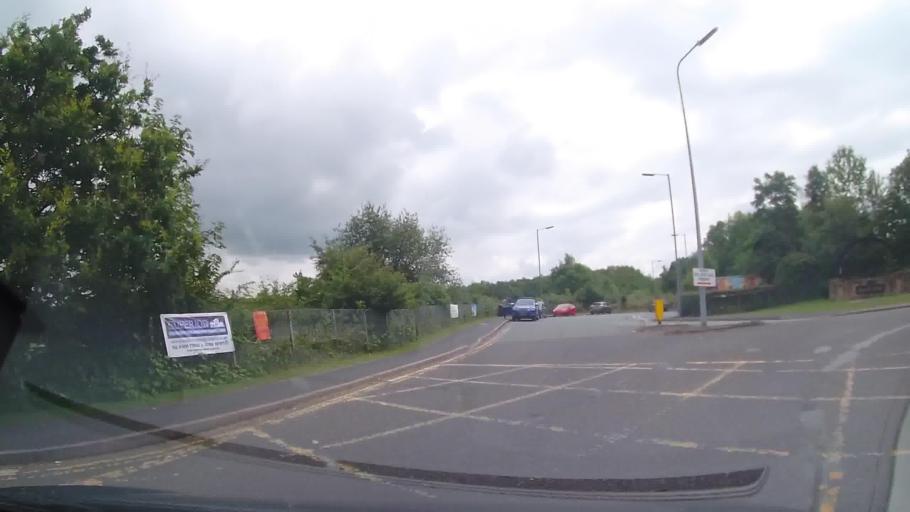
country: GB
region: Wales
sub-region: Wrexham
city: Chirk
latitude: 52.9507
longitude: -3.0417
